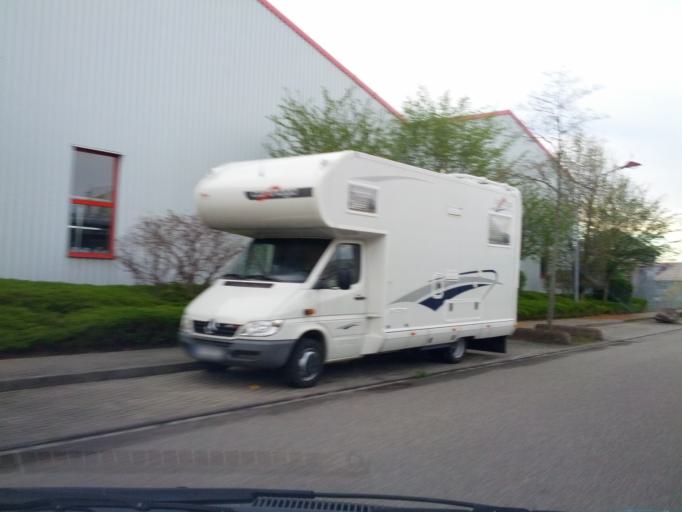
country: DE
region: Baden-Wuerttemberg
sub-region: Freiburg Region
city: Bad Krozingen
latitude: 47.9217
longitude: 7.7247
